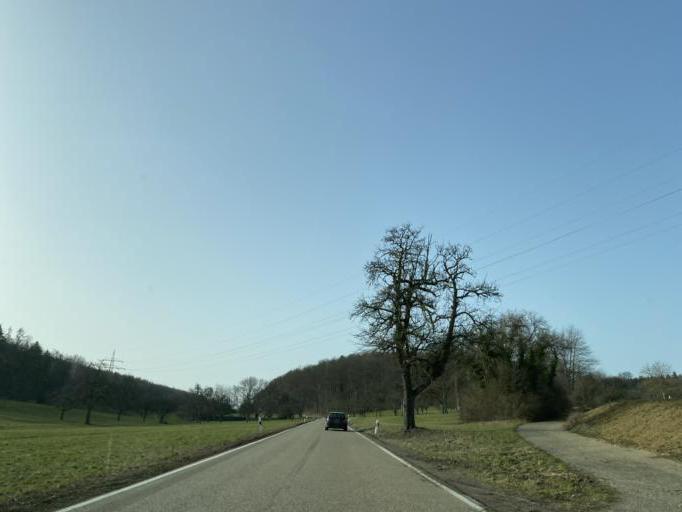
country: DE
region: Baden-Wuerttemberg
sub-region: Karlsruhe Region
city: Wiernsheim
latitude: 48.8877
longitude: 8.8431
